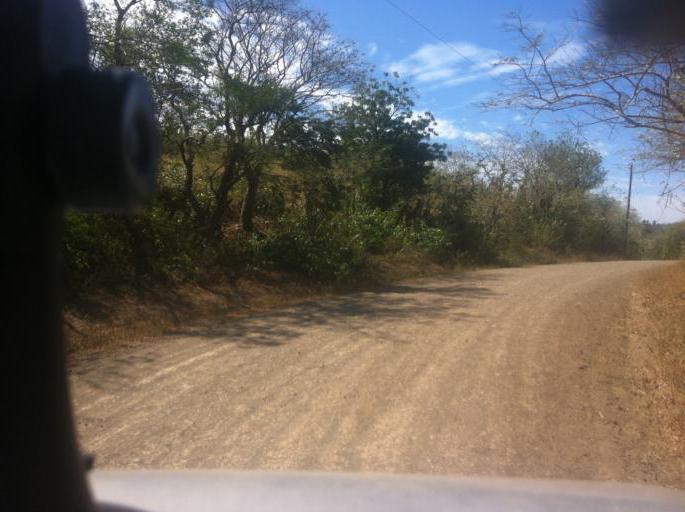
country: NI
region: Rivas
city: Tola
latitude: 11.5371
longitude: -86.0457
